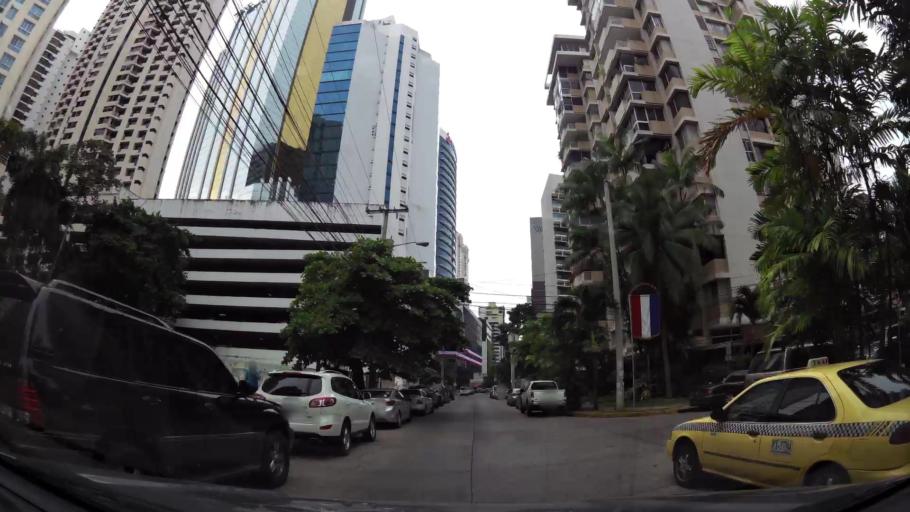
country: PA
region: Panama
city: Panama
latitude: 8.9777
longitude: -79.5214
